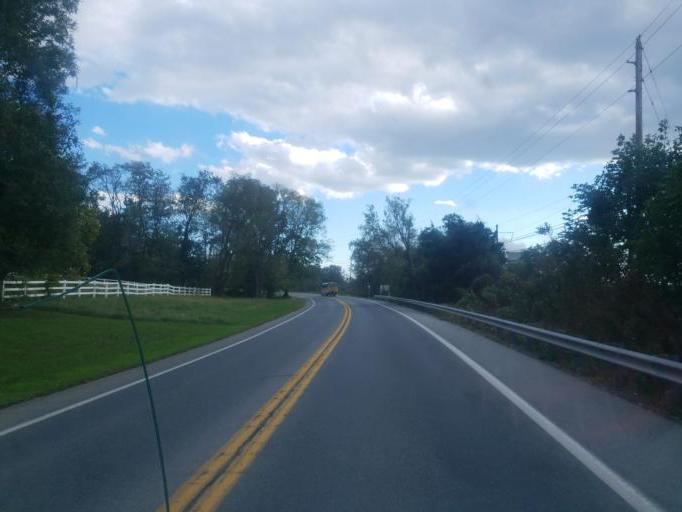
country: US
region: Pennsylvania
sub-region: Dauphin County
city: Middletown
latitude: 40.1709
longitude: -76.7232
